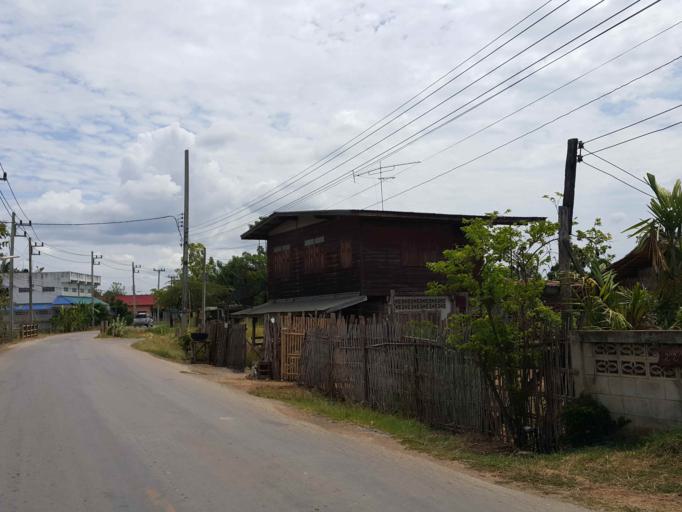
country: TH
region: Sukhothai
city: Thung Saliam
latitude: 17.3270
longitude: 99.5494
